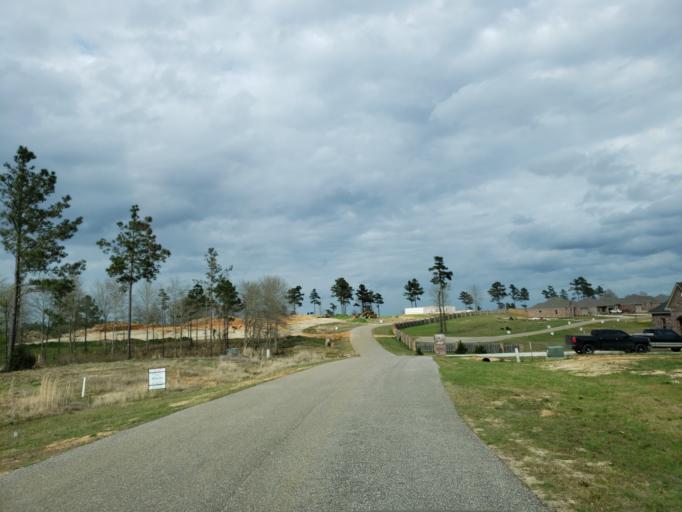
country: US
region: Mississippi
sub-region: Jones County
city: Ellisville
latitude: 31.5566
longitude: -89.2580
